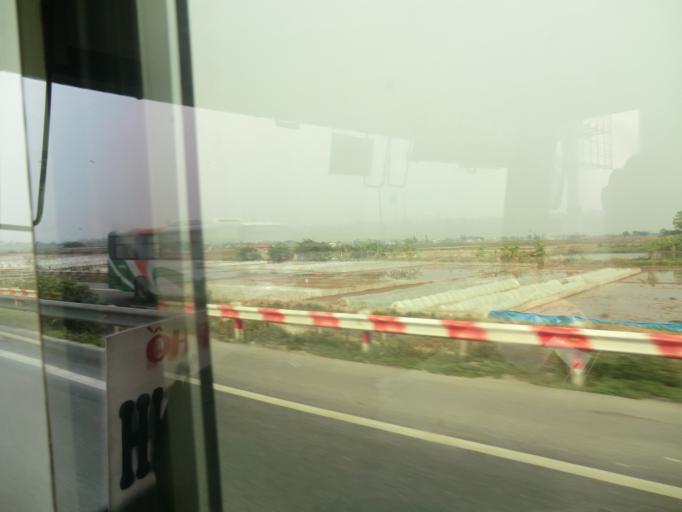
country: VN
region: Ha Noi
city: Thuong Tin
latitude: 20.8365
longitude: 105.8871
